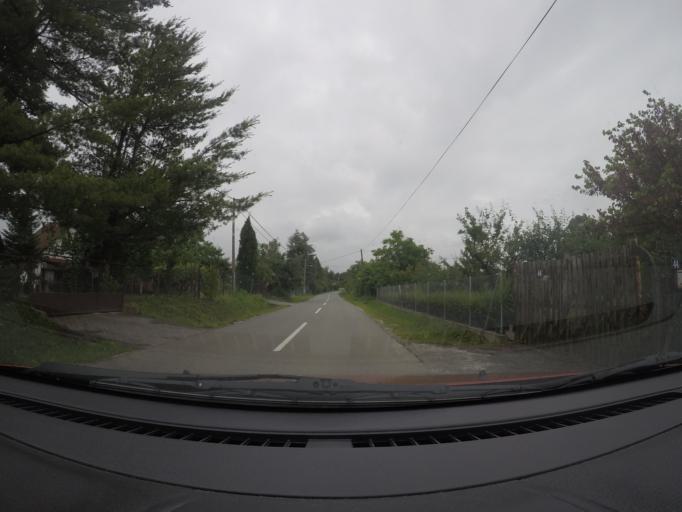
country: RS
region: Central Serbia
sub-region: Belgrade
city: Sopot
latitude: 44.5214
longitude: 20.5306
